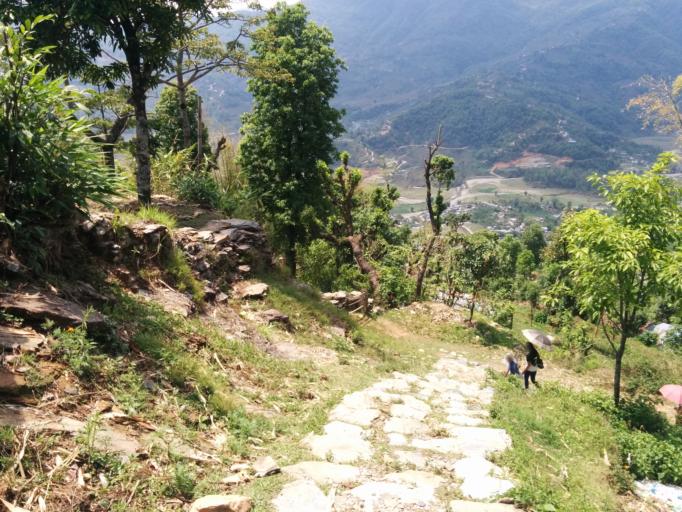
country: NP
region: Western Region
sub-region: Gandaki Zone
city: Pokhara
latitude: 28.1980
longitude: 83.9512
